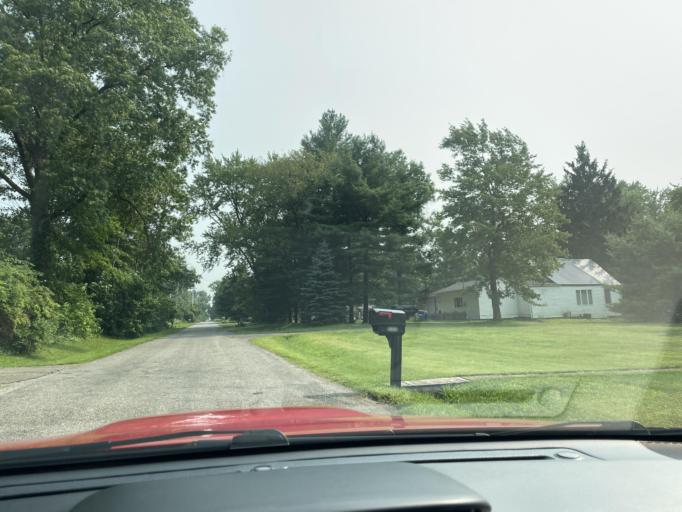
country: US
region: Ohio
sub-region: Trumbull County
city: McDonald
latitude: 41.1632
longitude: -80.7365
